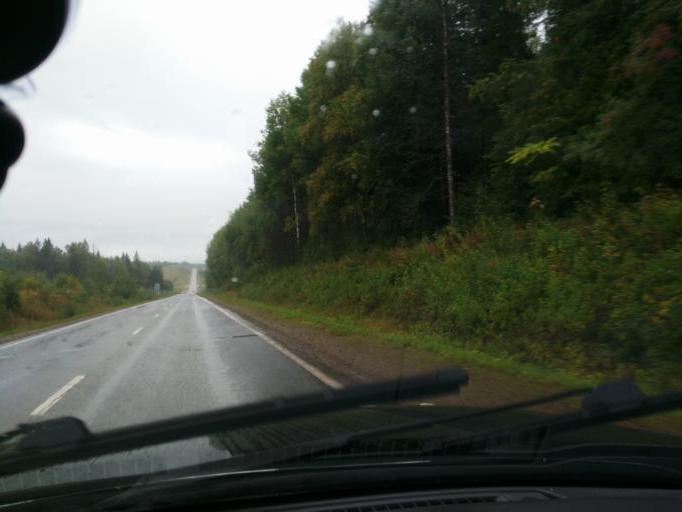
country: RU
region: Perm
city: Osa
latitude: 57.4142
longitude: 55.6229
